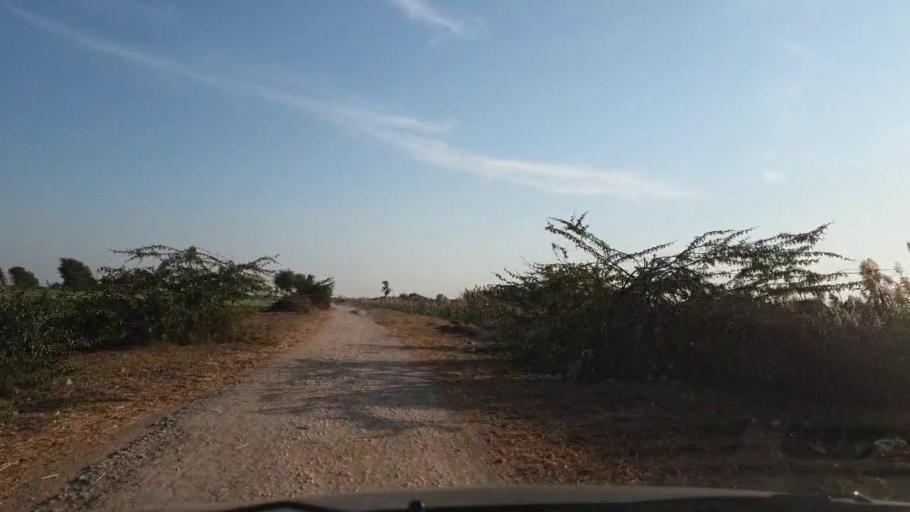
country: PK
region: Sindh
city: Khadro
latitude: 26.2165
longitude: 68.7413
